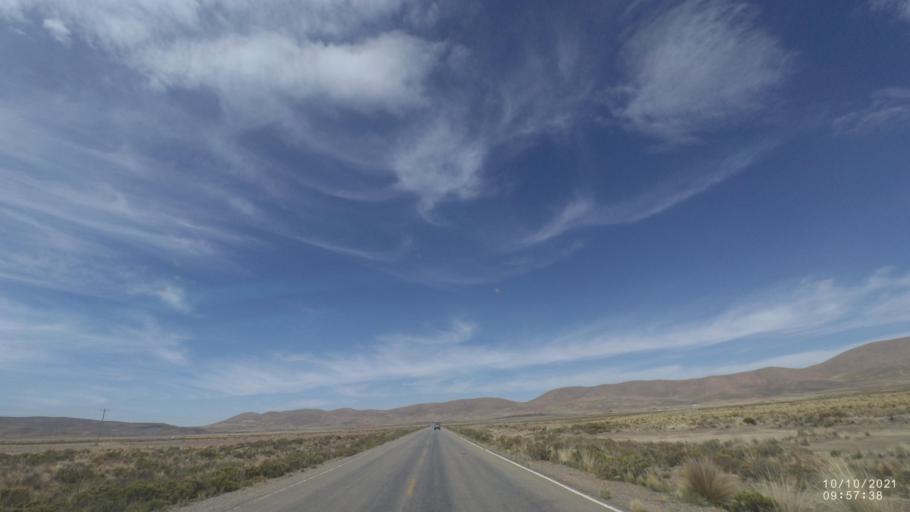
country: BO
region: La Paz
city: Colquiri
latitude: -17.3393
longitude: -67.3871
